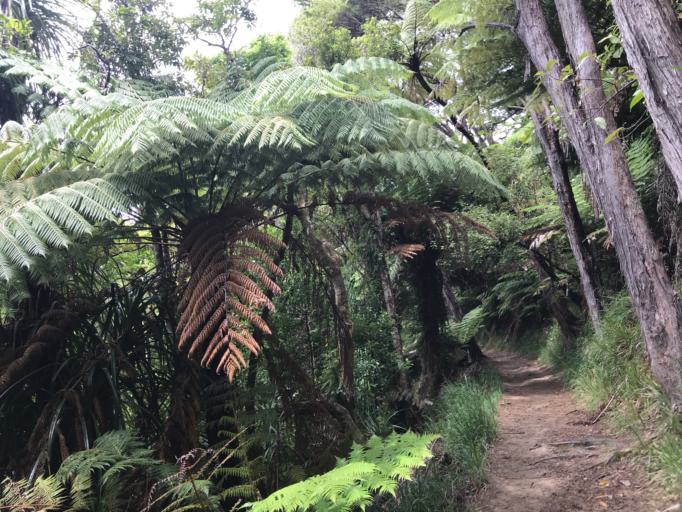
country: NZ
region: Marlborough
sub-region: Marlborough District
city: Picton
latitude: -41.2485
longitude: 173.9547
